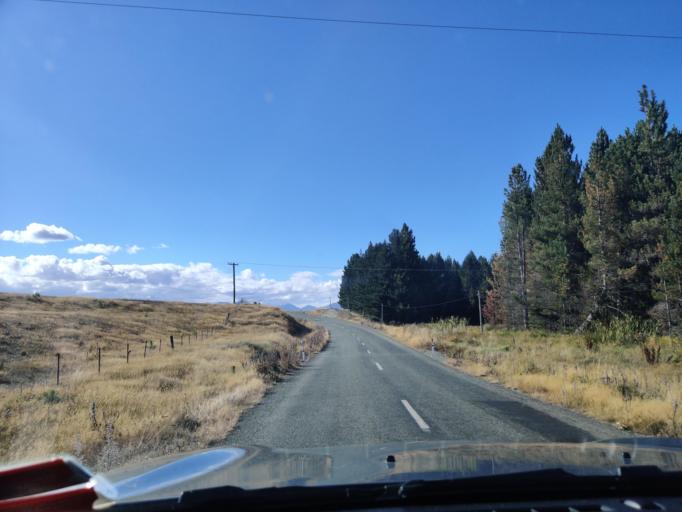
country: NZ
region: Canterbury
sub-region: Timaru District
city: Pleasant Point
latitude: -43.9996
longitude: 170.4505
